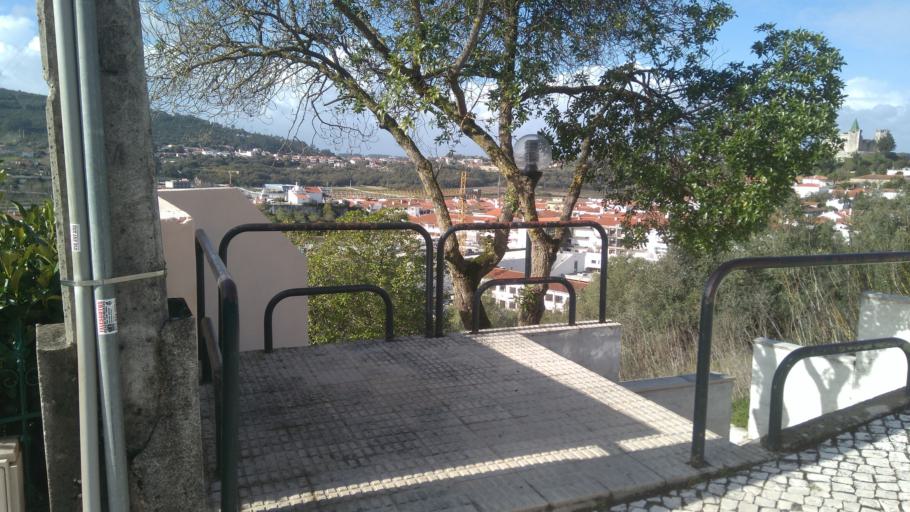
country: PT
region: Leiria
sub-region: Porto de Mos
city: Porto de Mos
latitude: 39.5997
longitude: -8.8141
